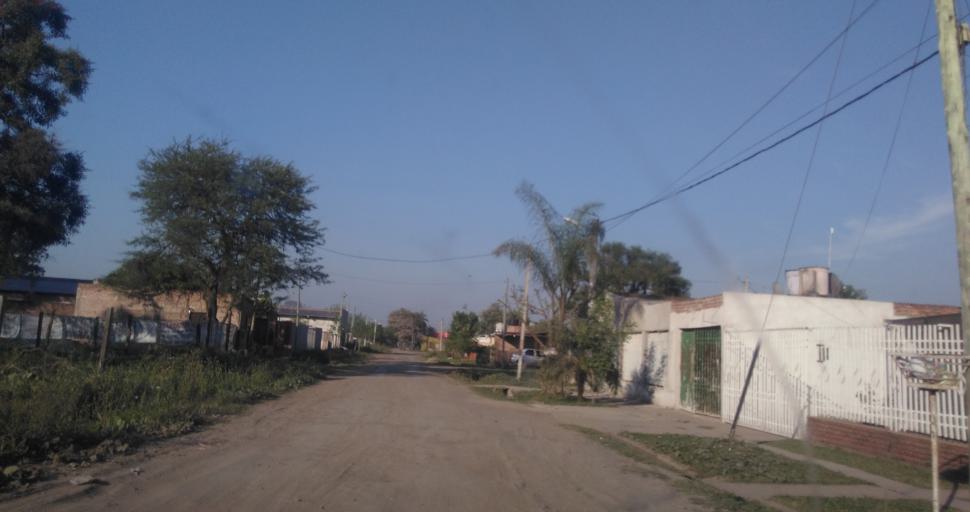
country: AR
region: Chaco
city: Fontana
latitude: -27.4147
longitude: -59.0350
